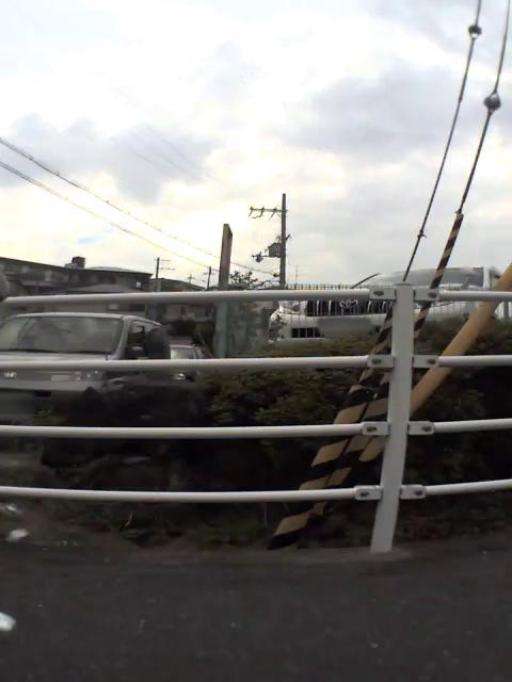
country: JP
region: Osaka
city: Hirakata
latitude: 34.8025
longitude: 135.6447
